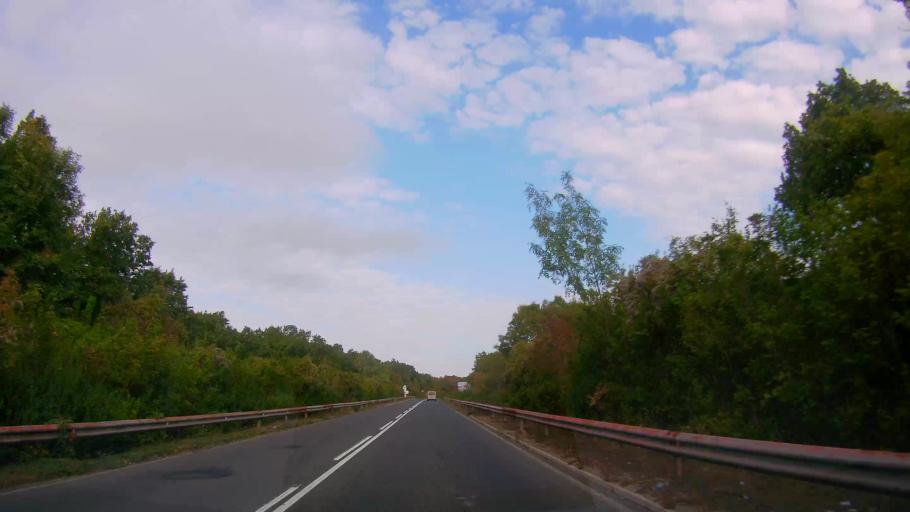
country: BG
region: Burgas
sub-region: Obshtina Primorsko
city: Primorsko
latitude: 42.3355
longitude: 27.7211
